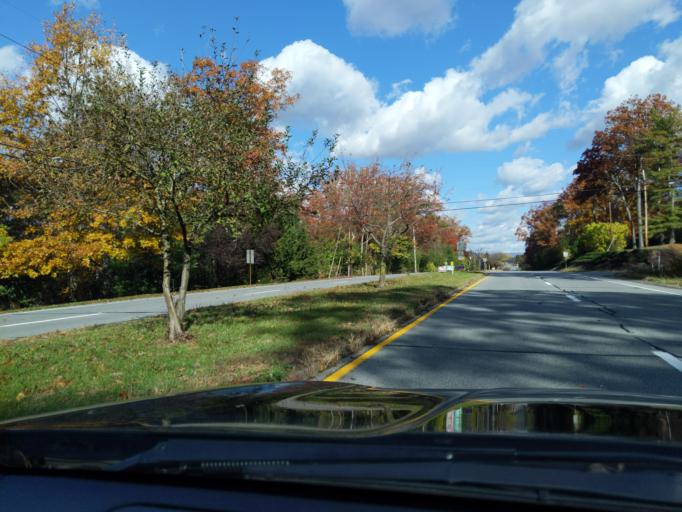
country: US
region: Pennsylvania
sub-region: Blair County
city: Hollidaysburg
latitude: 40.4447
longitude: -78.3931
